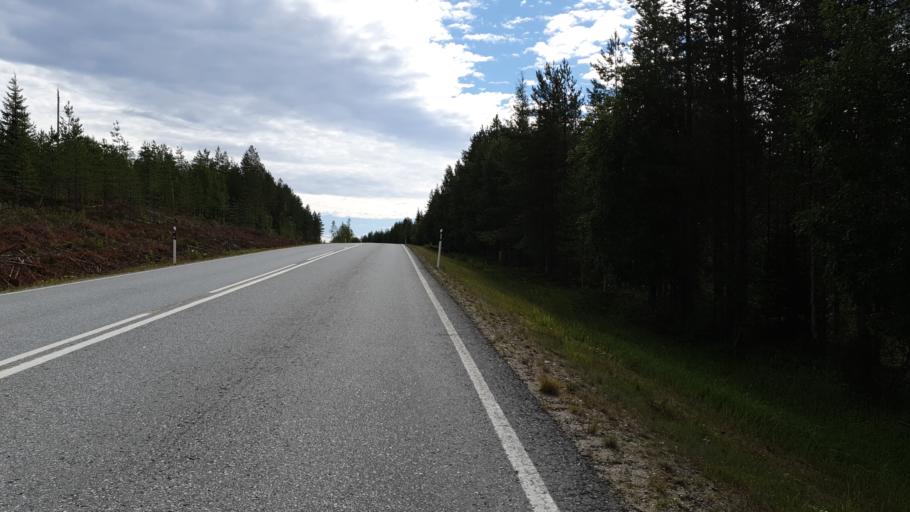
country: FI
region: Kainuu
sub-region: Kehys-Kainuu
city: Kuhmo
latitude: 64.4905
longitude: 29.8512
